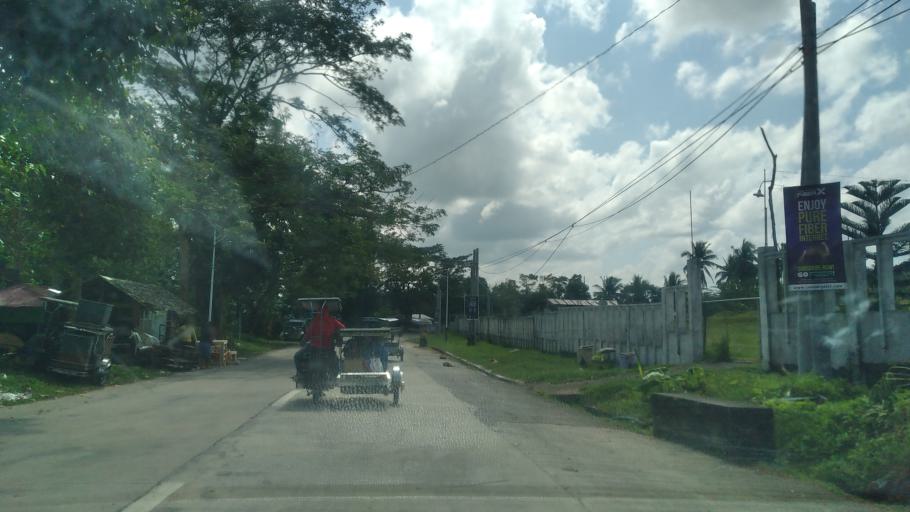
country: PH
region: Calabarzon
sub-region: Province of Quezon
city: Macalelon
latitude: 13.7579
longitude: 122.1425
